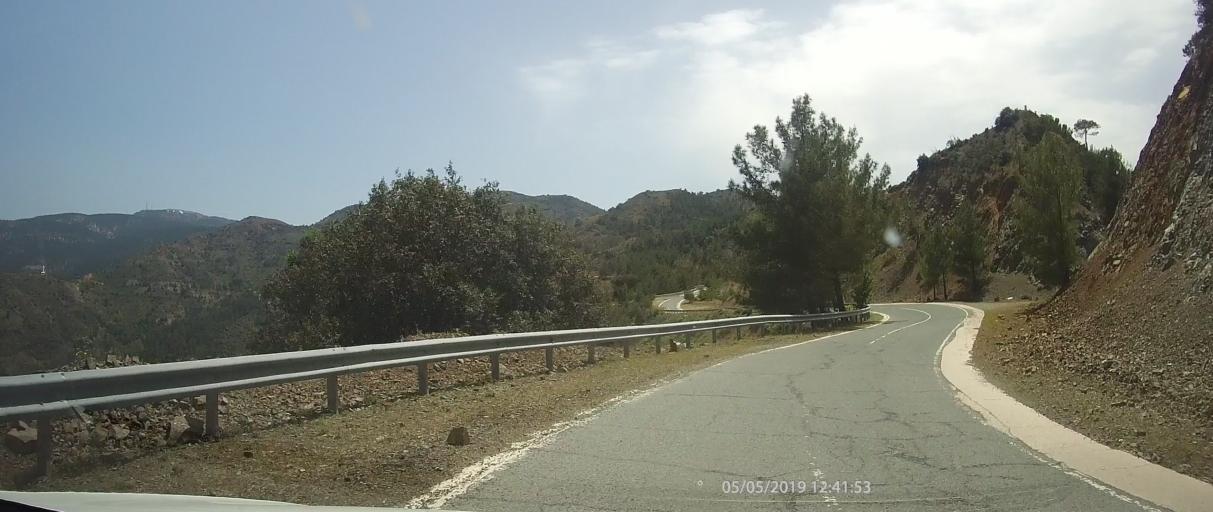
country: CY
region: Lefkosia
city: Kakopetria
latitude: 34.9788
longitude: 32.8095
